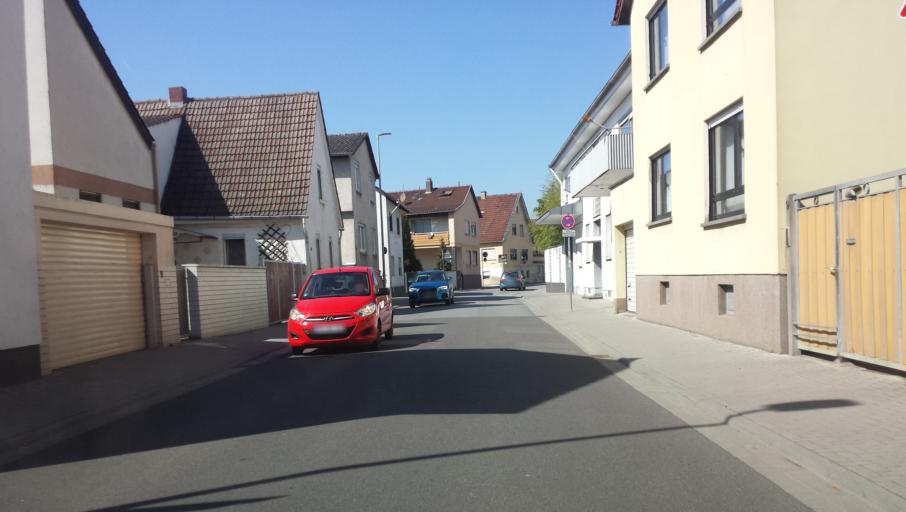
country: DE
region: Hesse
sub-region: Regierungsbezirk Darmstadt
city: Biblis
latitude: 49.6832
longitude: 8.4500
